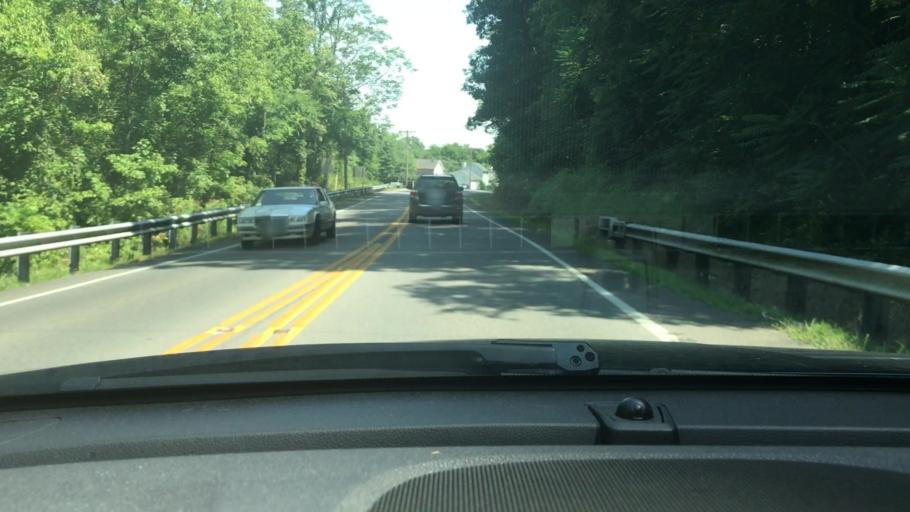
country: US
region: Tennessee
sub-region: Sumner County
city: Shackle Island
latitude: 36.3674
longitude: -86.6152
